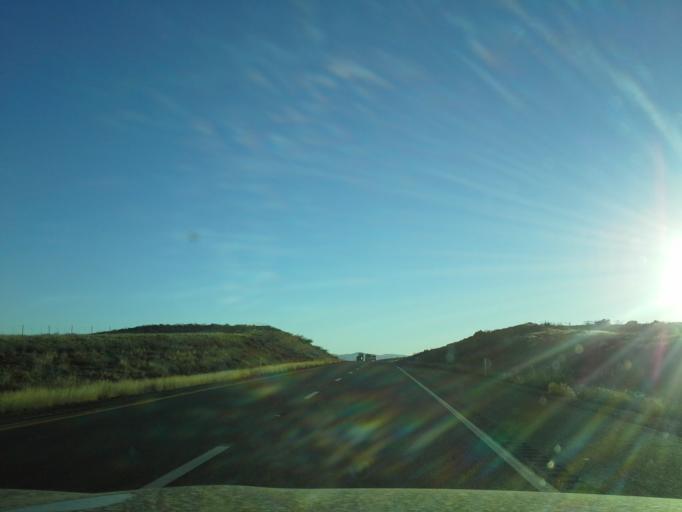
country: US
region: Arizona
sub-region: Yavapai County
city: Cordes Lakes
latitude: 34.4415
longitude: -112.0404
